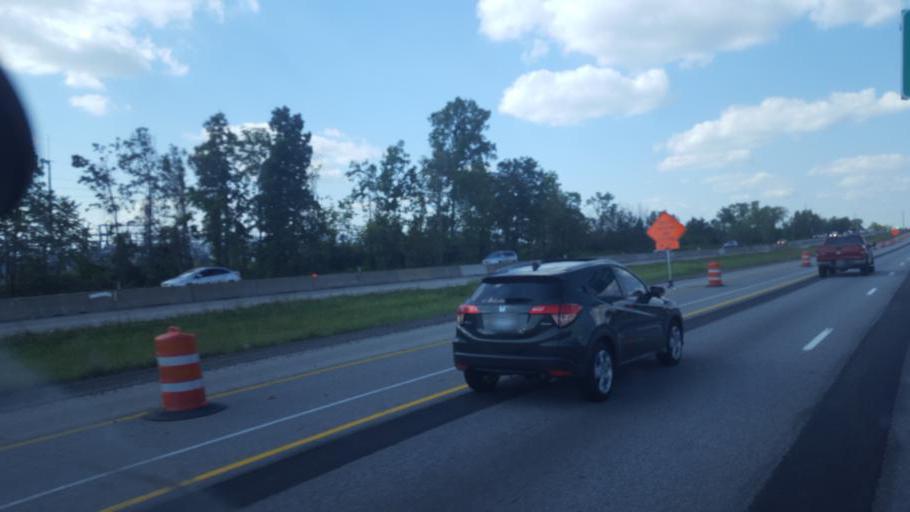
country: US
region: Ohio
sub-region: Franklin County
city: Hilliard
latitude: 40.0583
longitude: -83.1306
